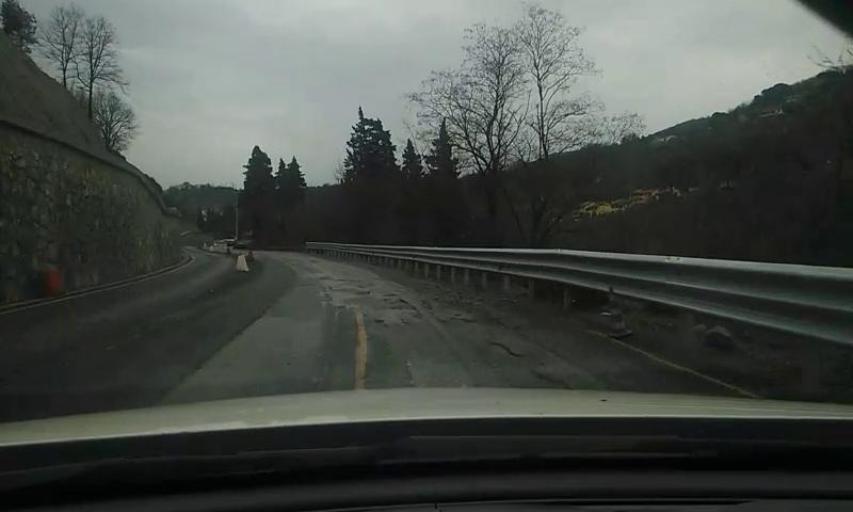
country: IT
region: Tuscany
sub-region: Provincia di Prato
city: Vaiano
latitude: 43.9238
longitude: 11.1266
